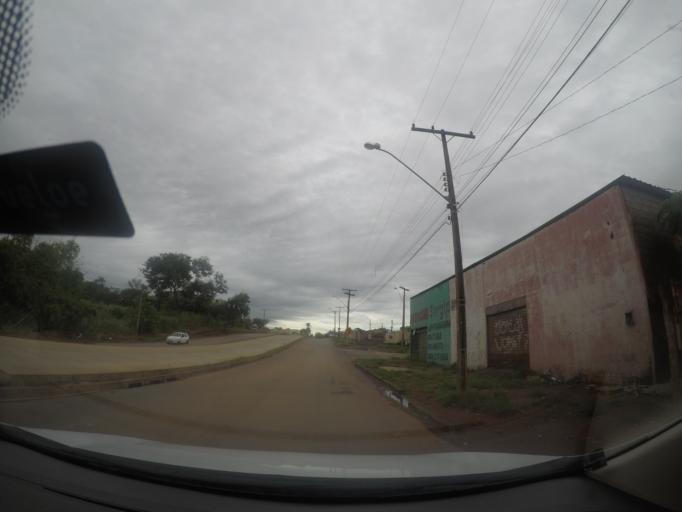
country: BR
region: Goias
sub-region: Goiania
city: Goiania
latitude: -16.6172
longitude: -49.3091
